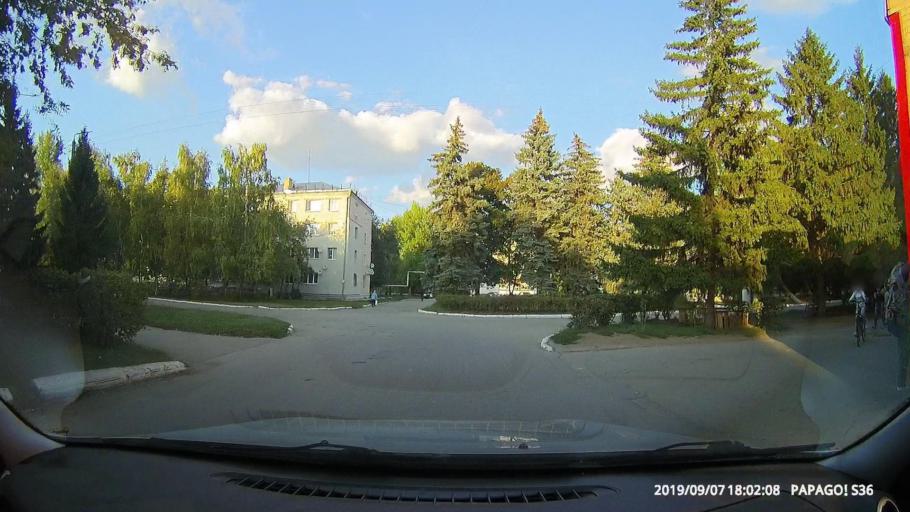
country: RU
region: Samara
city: Chapayevsk
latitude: 52.9905
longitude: 49.7769
